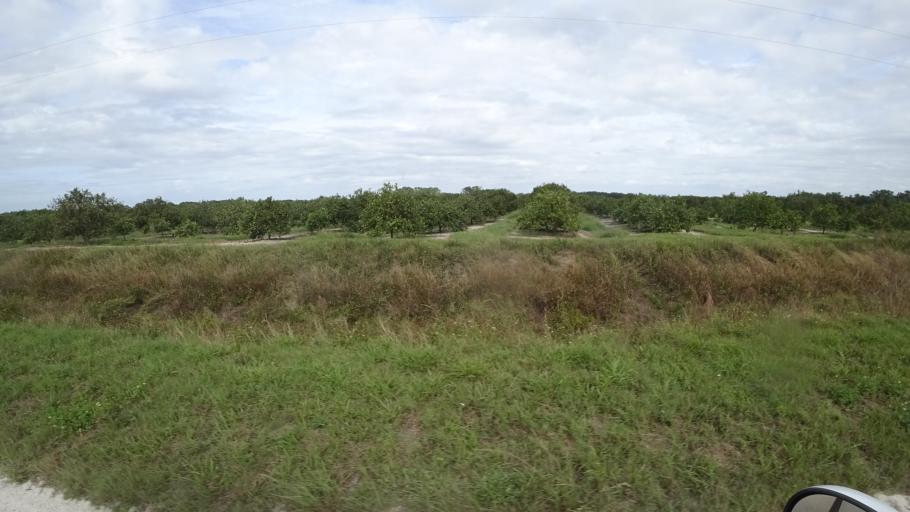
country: US
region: Florida
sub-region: Hillsborough County
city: Wimauma
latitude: 27.6229
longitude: -82.2867
